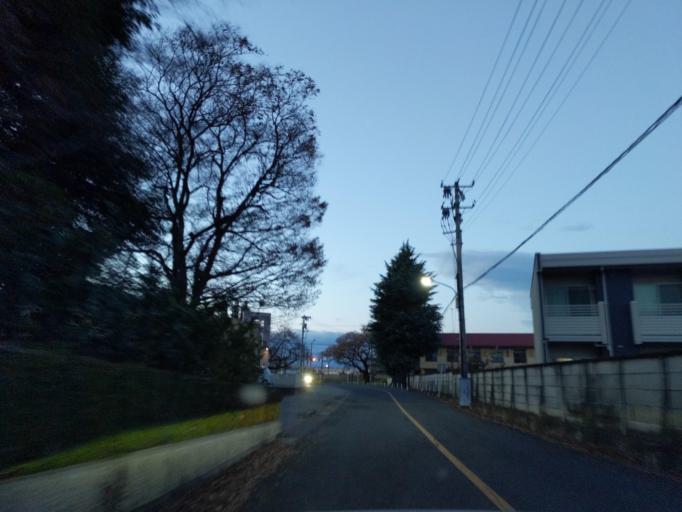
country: JP
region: Fukushima
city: Koriyama
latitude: 37.3614
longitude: 140.3833
